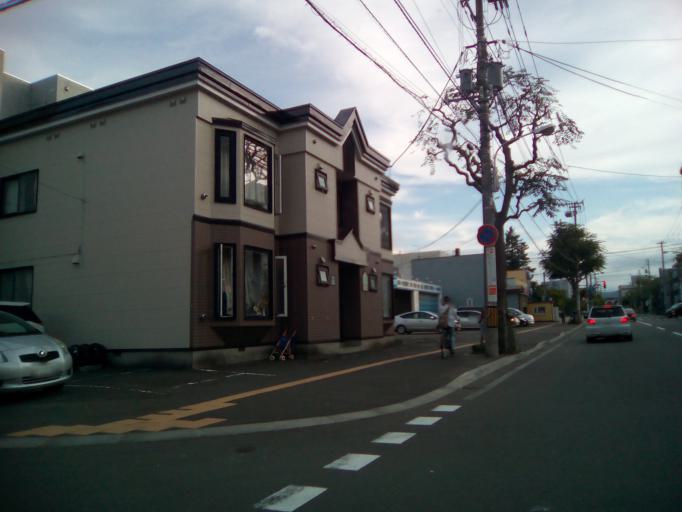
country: JP
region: Hokkaido
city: Sapporo
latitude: 43.0464
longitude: 141.3777
